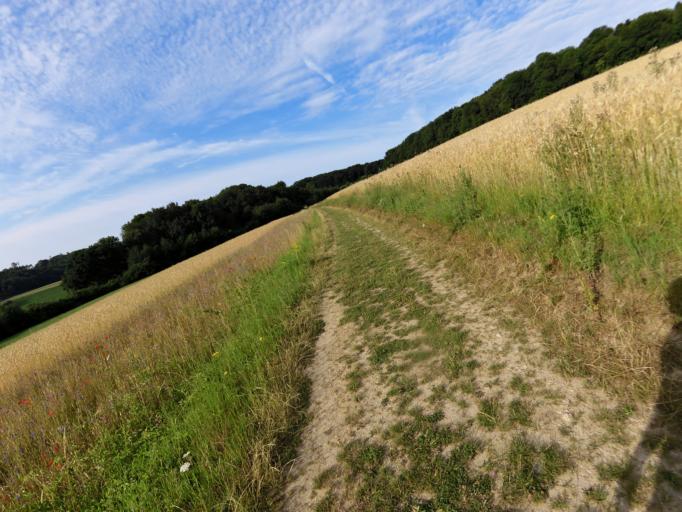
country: NL
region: Limburg
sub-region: Valkenburg aan de Geul
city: Schin op Geul
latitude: 50.8491
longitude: 5.8533
